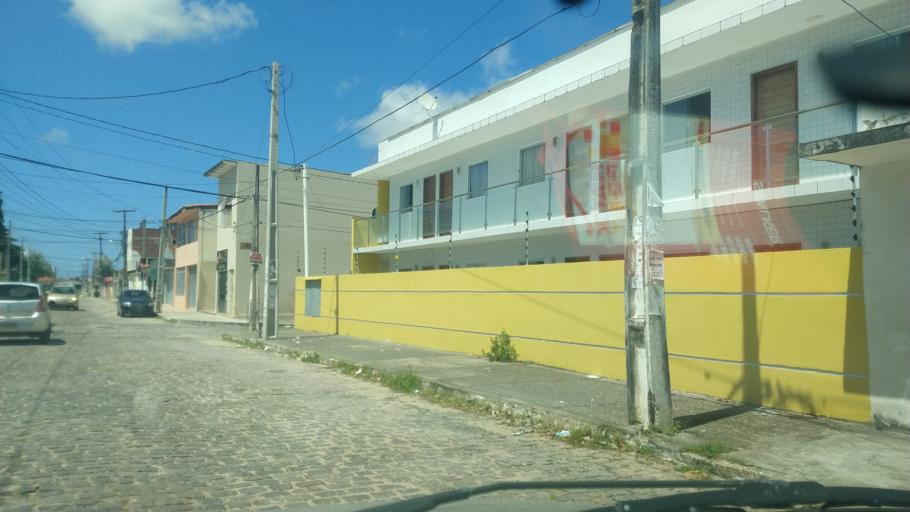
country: BR
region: Rio Grande do Norte
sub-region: Natal
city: Natal
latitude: -5.8565
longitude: -35.2106
